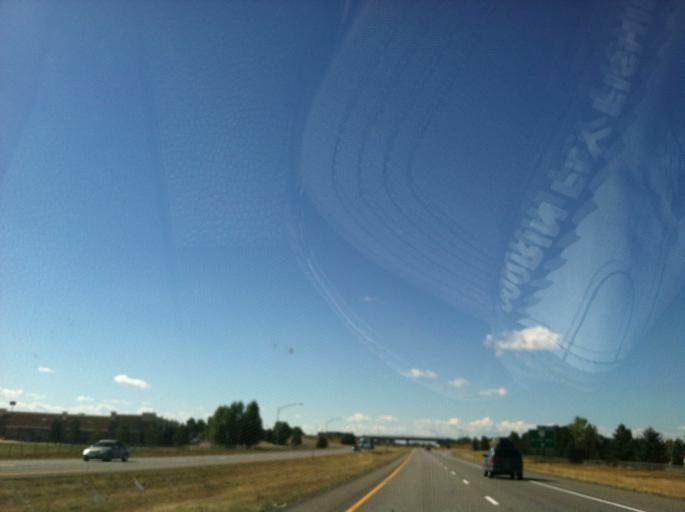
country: US
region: Montana
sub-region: Gallatin County
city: Bozeman
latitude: 45.6959
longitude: -111.0404
